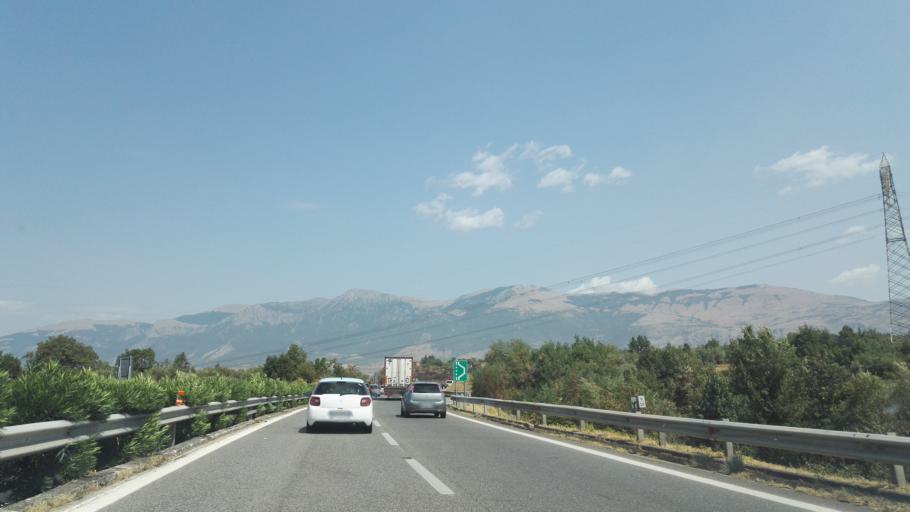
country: IT
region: Calabria
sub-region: Provincia di Cosenza
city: Castrovillari
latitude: 39.7765
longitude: 16.2230
